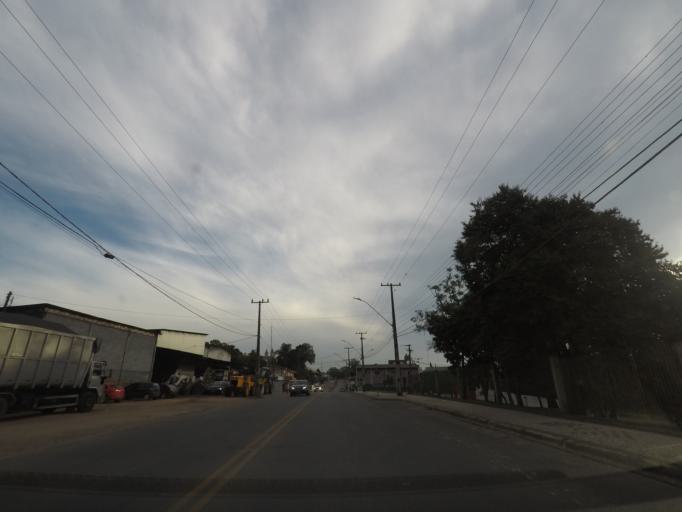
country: BR
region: Parana
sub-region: Colombo
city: Colombo
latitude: -25.2900
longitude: -49.2193
